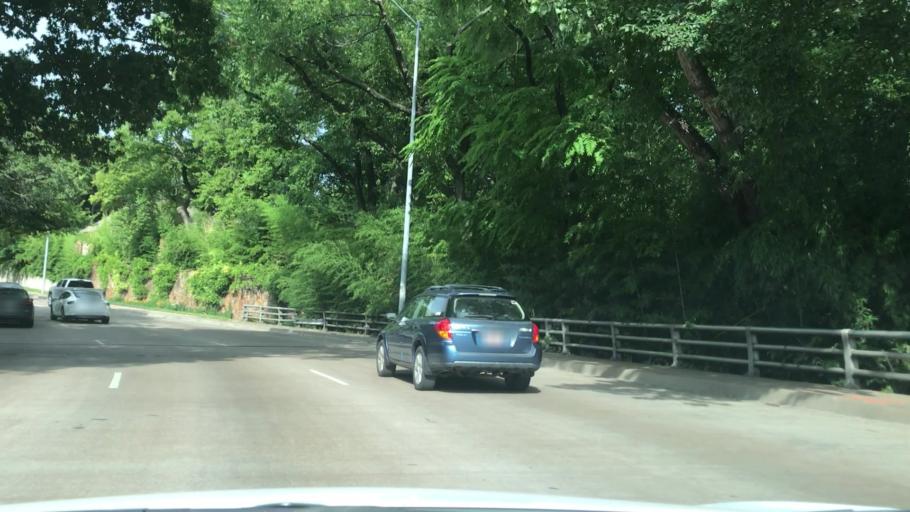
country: US
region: Texas
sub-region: Dallas County
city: Highland Park
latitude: 32.8174
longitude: -96.7989
